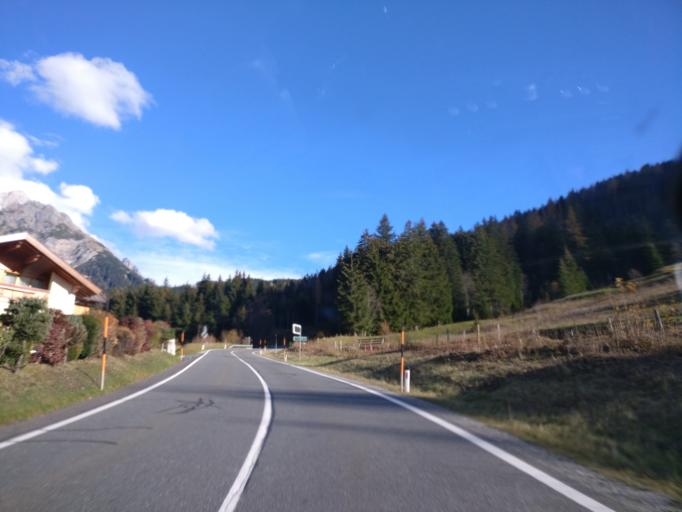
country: AT
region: Salzburg
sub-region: Politischer Bezirk Zell am See
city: Dienten am Hochkonig
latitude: 47.4061
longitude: 12.9738
